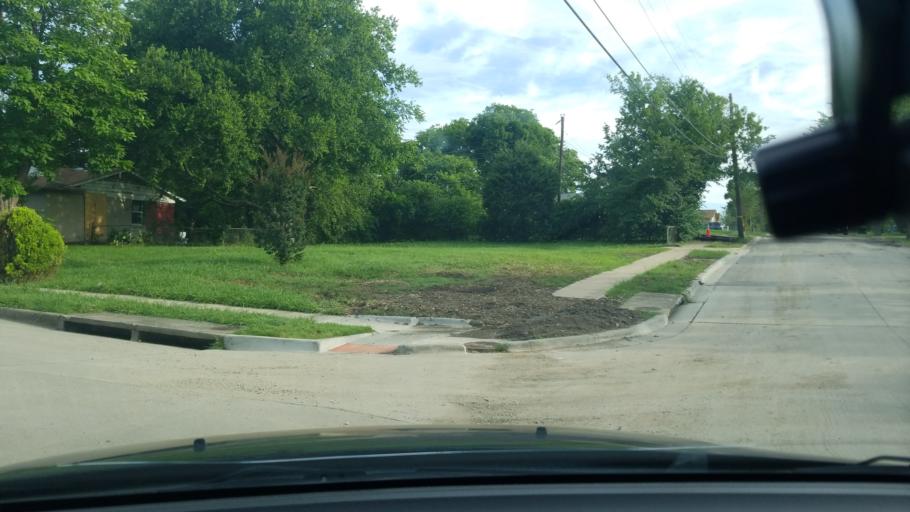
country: US
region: Texas
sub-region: Dallas County
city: Mesquite
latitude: 32.7581
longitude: -96.6236
